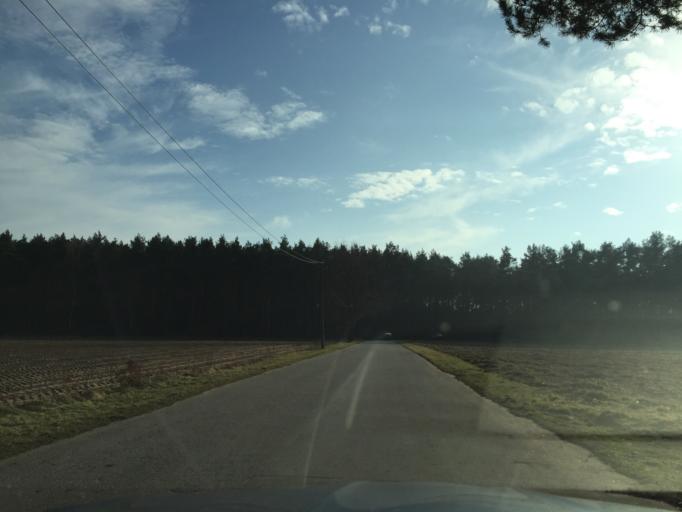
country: DE
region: Baden-Wuerttemberg
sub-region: Karlsruhe Region
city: Oftersheim
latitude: 49.3518
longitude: 8.6076
